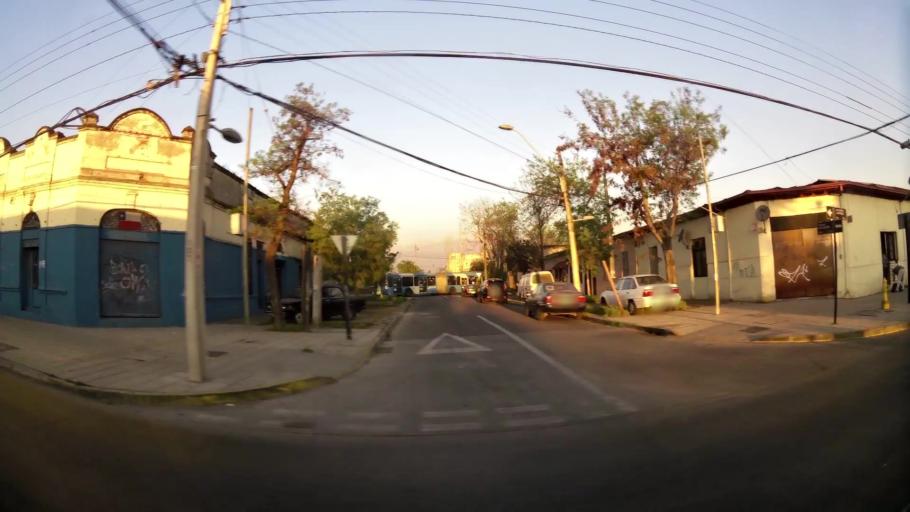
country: CL
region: Santiago Metropolitan
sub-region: Provincia de Santiago
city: Santiago
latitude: -33.4672
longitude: -70.6716
